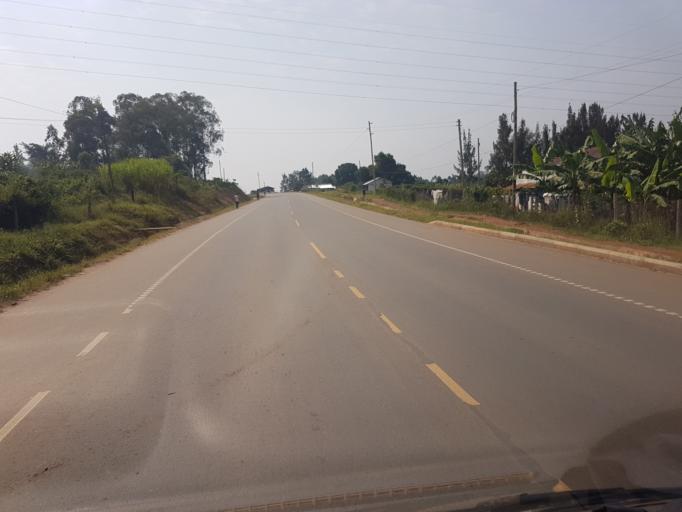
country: UG
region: Western Region
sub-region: Mbarara District
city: Bwizibwera
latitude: -0.6365
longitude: 30.6081
